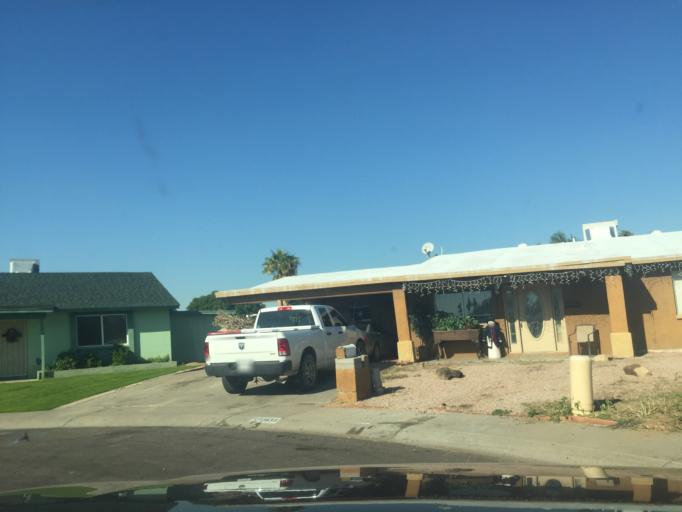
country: US
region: Arizona
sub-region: Maricopa County
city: Tolleson
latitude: 33.4793
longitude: -112.2148
